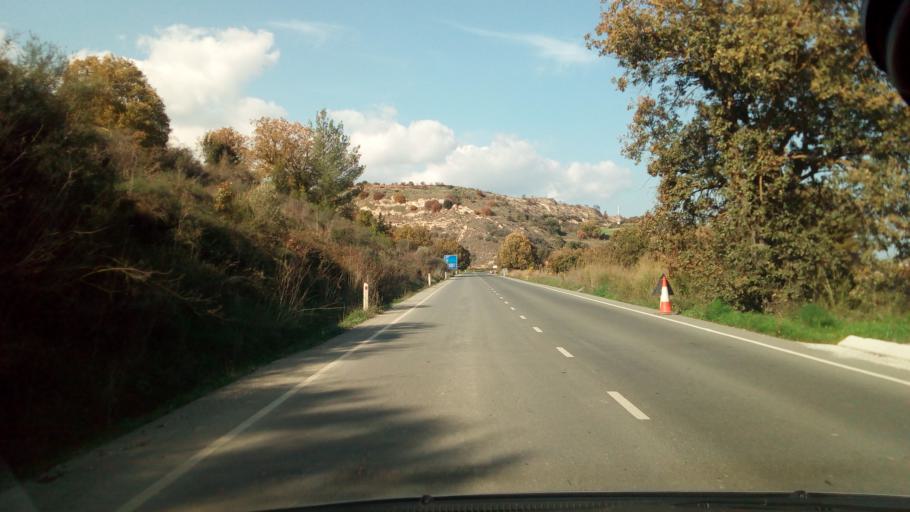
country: CY
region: Pafos
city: Polis
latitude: 34.9606
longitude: 32.4592
